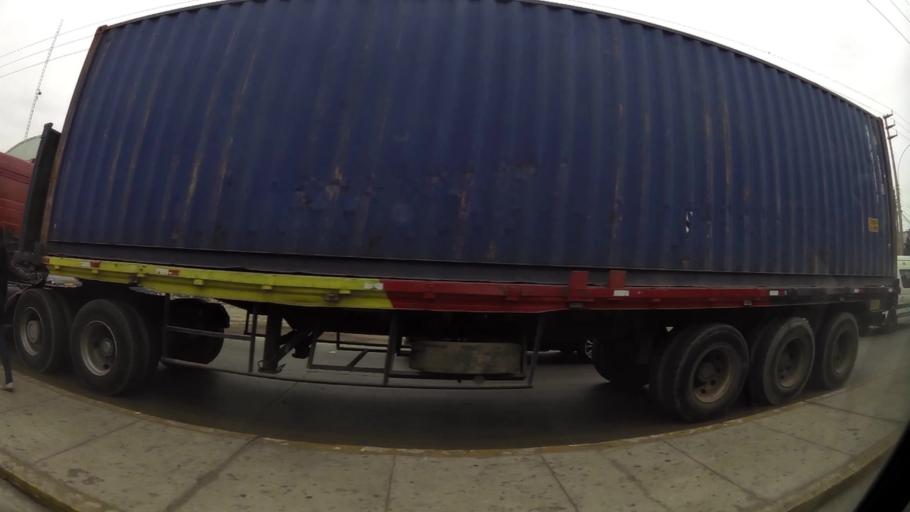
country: PE
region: Callao
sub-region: Callao
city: Callao
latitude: -12.0485
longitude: -77.0998
